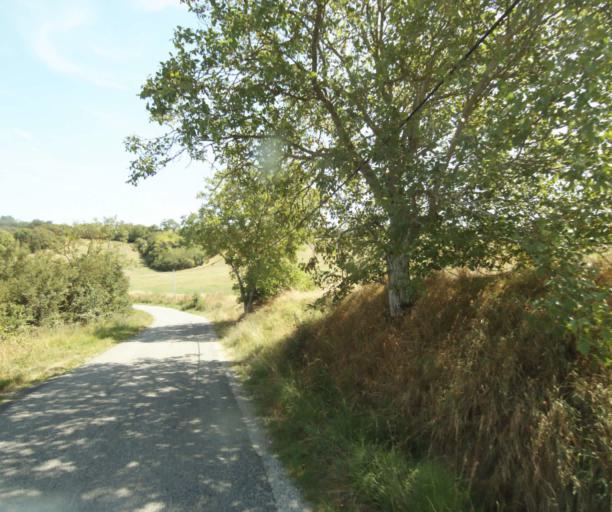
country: FR
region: Midi-Pyrenees
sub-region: Departement de l'Ariege
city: Lezat-sur-Leze
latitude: 43.2427
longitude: 1.3989
